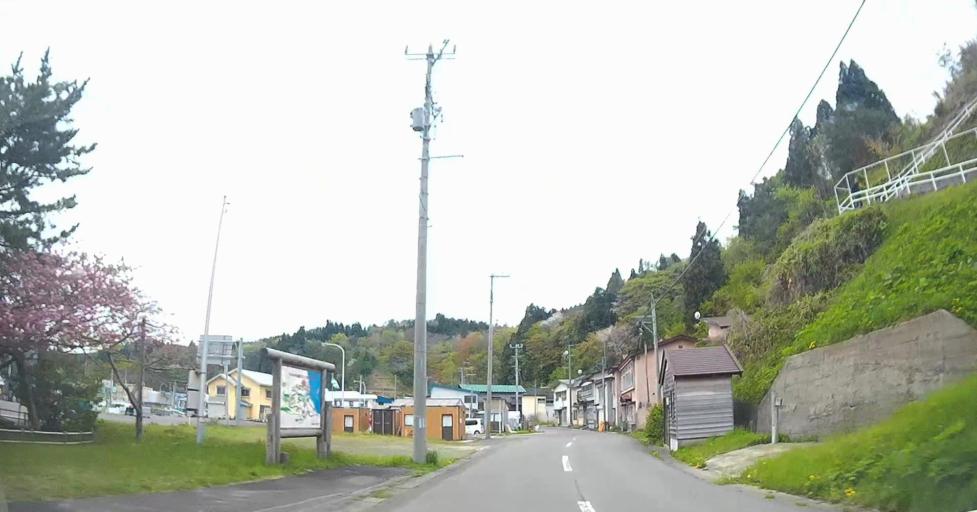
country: JP
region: Aomori
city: Shimokizukuri
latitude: 41.1987
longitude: 140.4301
